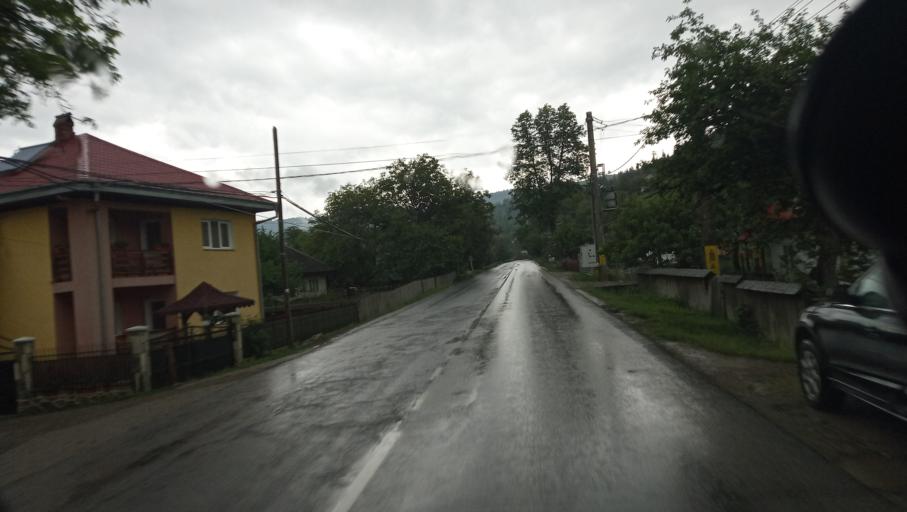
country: RO
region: Neamt
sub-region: Comuna Poiana Teiului
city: Poiana Teiului
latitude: 47.0956
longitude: 25.9796
